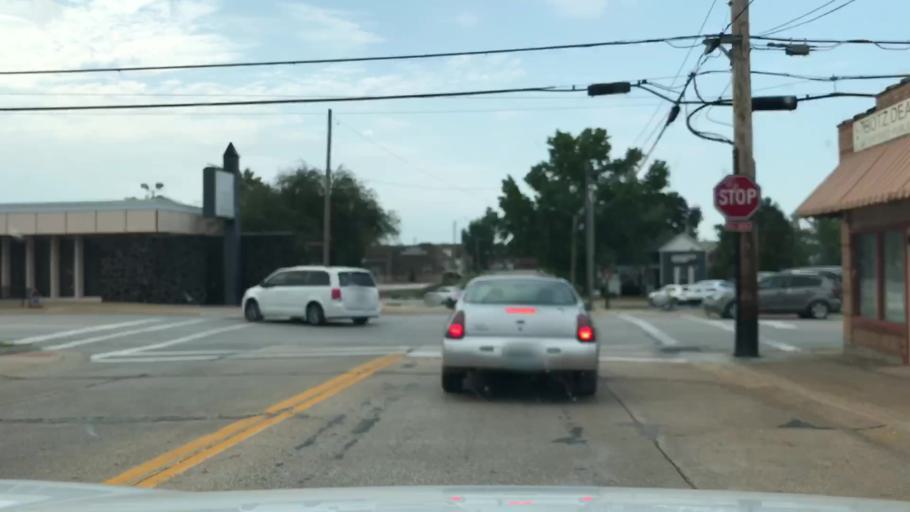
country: US
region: Missouri
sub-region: Saint Charles County
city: Wentzville
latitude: 38.8118
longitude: -90.8532
